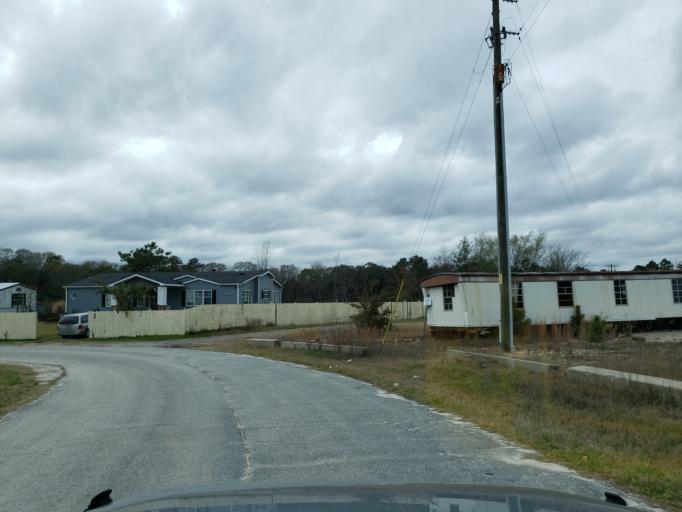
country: US
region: Georgia
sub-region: Chatham County
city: Bloomingdale
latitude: 32.0775
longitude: -81.3724
